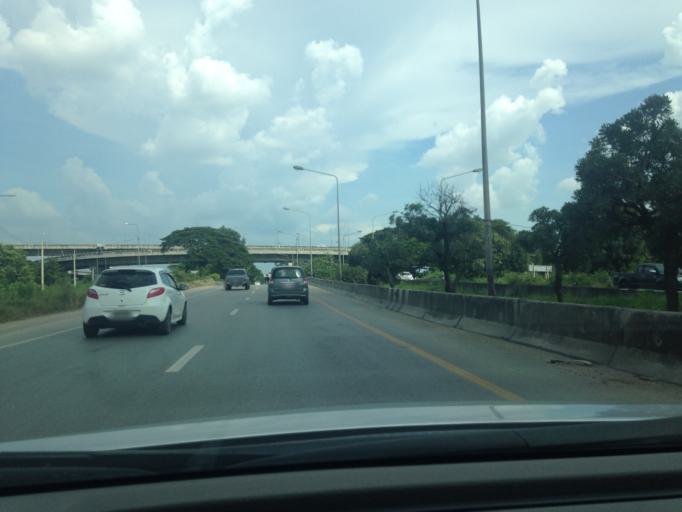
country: TH
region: Pathum Thani
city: Sam Khok
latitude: 14.0661
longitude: 100.5768
